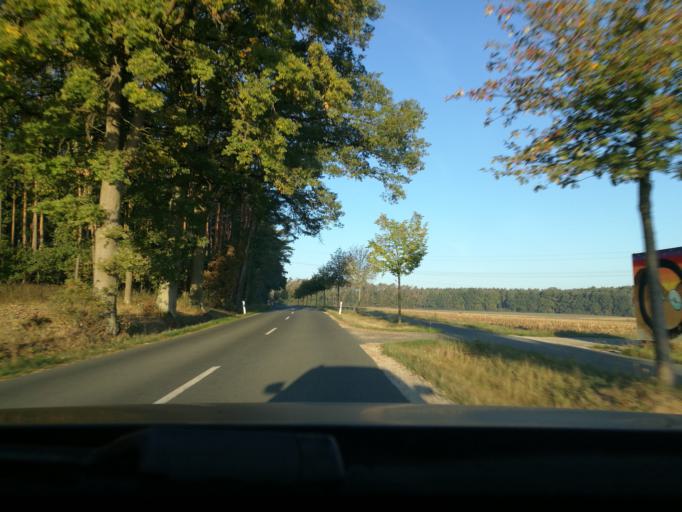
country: DE
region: Bavaria
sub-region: Regierungsbezirk Mittelfranken
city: Veitsbronn
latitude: 49.5293
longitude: 10.8905
